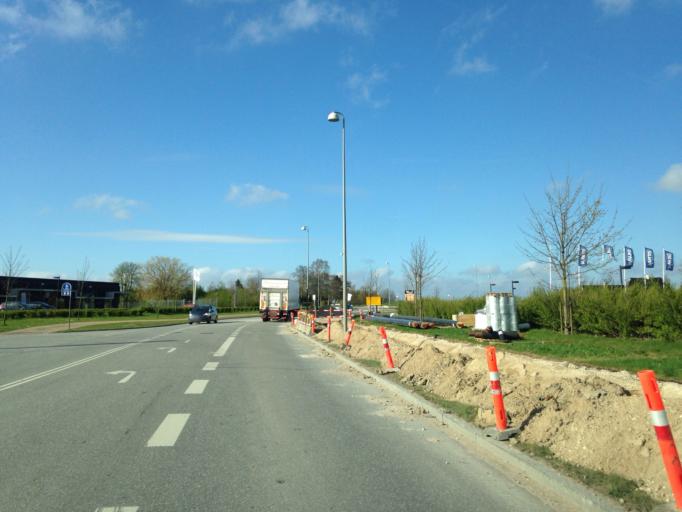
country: DK
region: Zealand
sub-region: Greve Kommune
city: Greve
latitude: 55.5923
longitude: 12.2671
